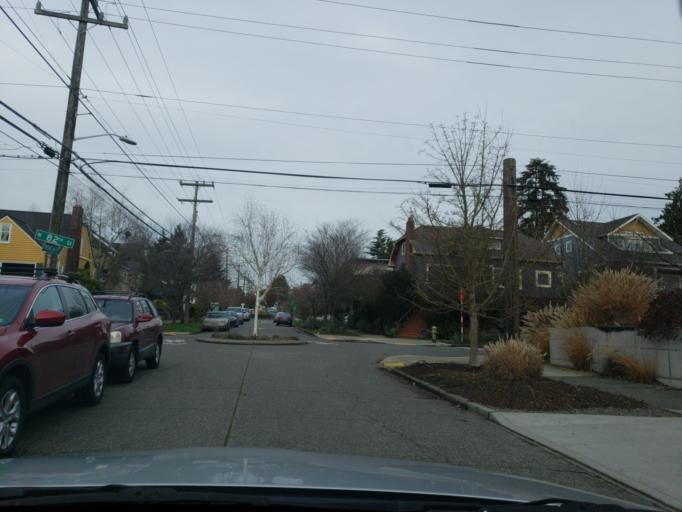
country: US
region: Washington
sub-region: King County
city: Shoreline
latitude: 47.6882
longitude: -122.3500
